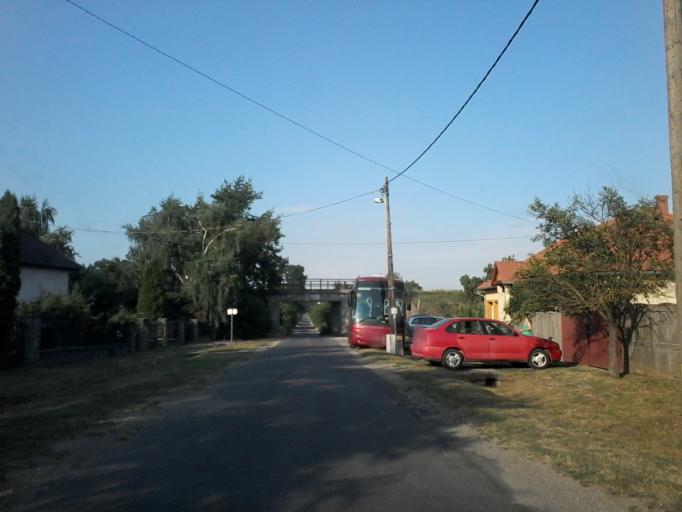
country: HU
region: Vas
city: Sarvar
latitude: 47.2168
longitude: 17.0185
